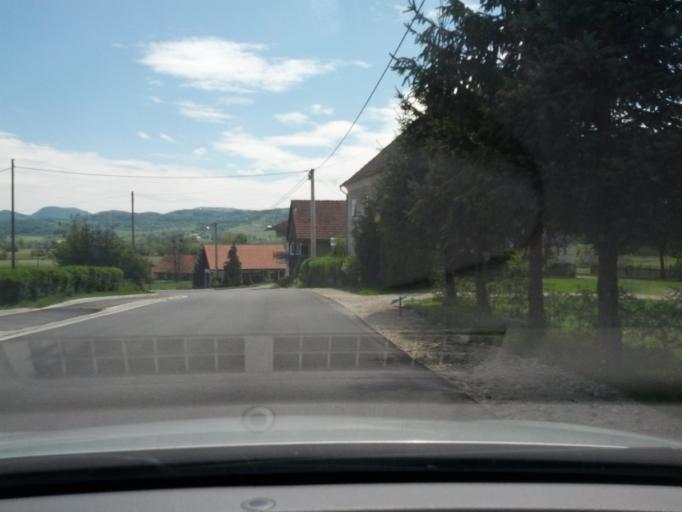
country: SI
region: Podcetrtek
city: Podcetrtek
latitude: 46.1136
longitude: 15.6125
